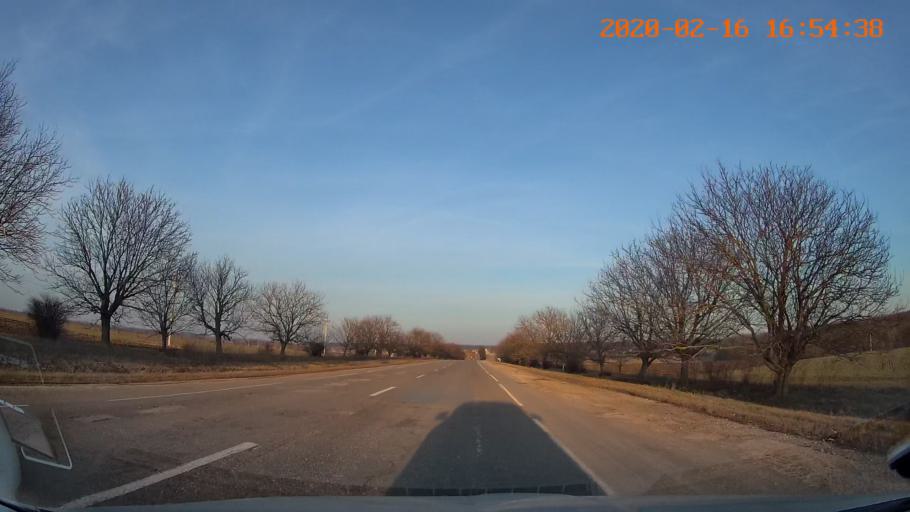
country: MD
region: Briceni
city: Briceni
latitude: 48.3227
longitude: 27.0112
